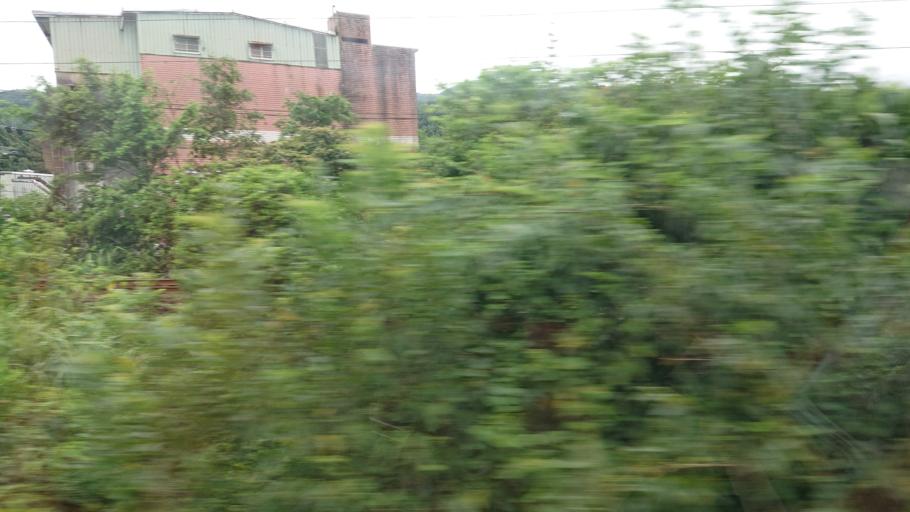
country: TW
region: Taiwan
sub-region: Keelung
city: Keelung
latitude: 25.1069
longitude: 121.8216
